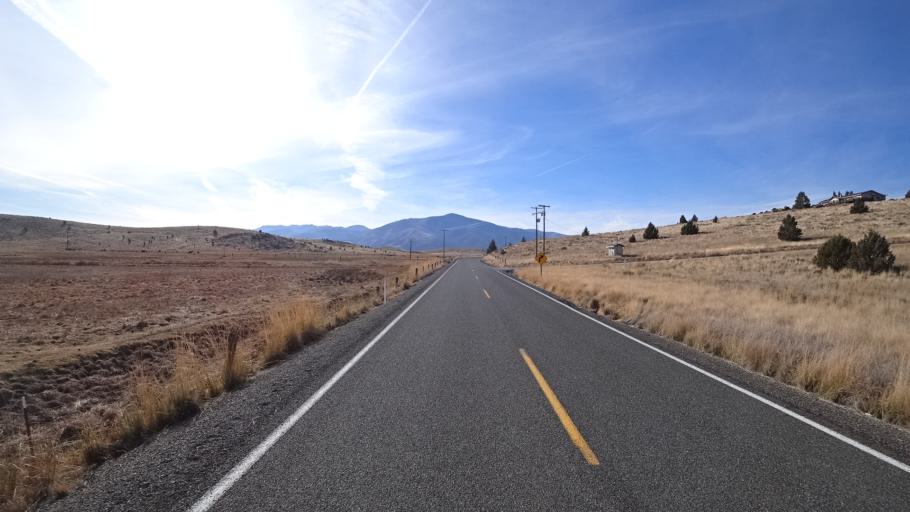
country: US
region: California
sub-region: Siskiyou County
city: Weed
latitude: 41.5391
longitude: -122.5036
